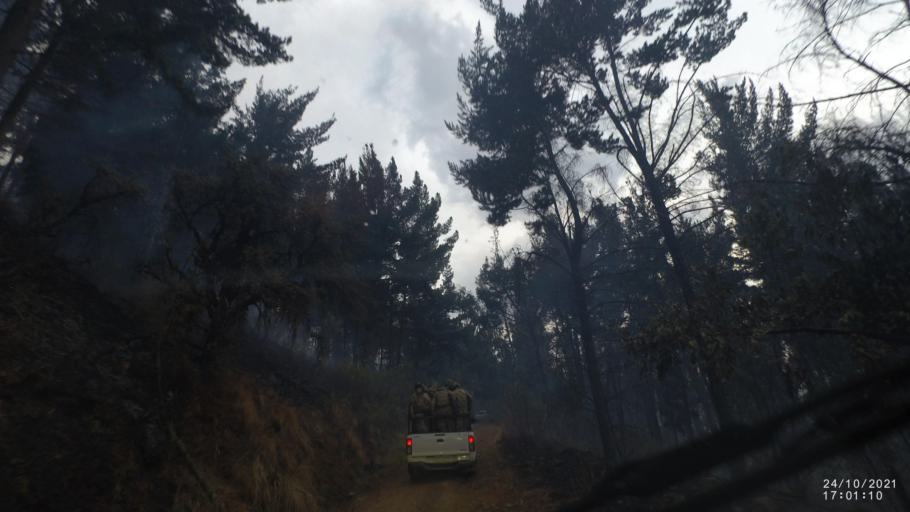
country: BO
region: Cochabamba
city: Cochabamba
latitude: -17.3382
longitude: -66.1417
